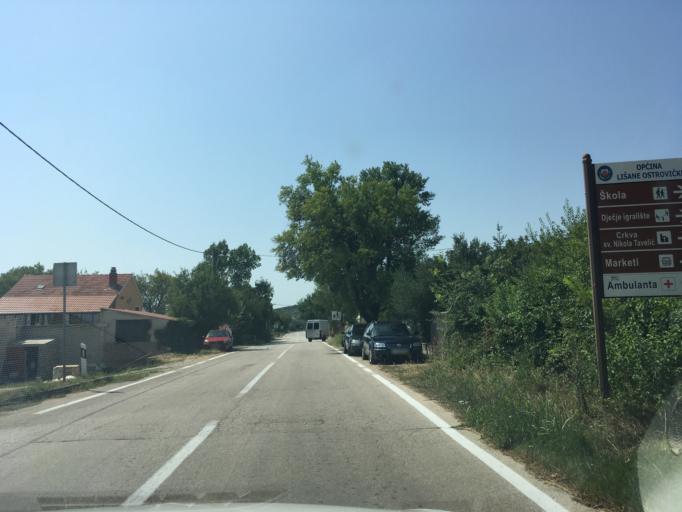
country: HR
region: Sibensko-Kniniska
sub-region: Grad Sibenik
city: Pirovac
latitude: 43.9612
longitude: 15.7671
